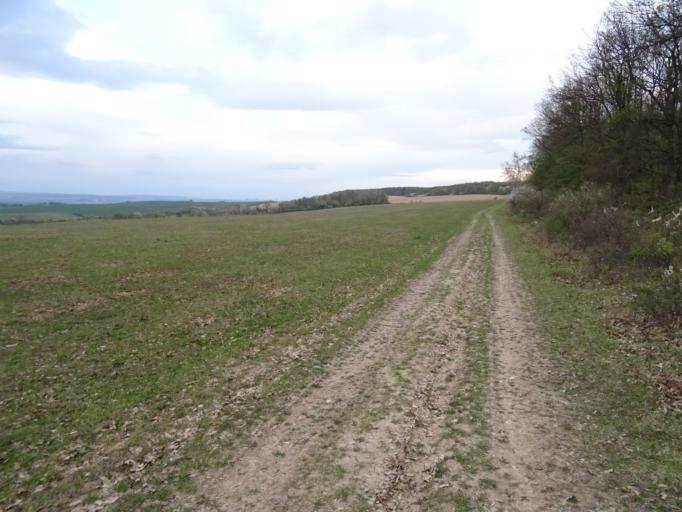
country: SK
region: Kosicky
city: Moldava nad Bodvou
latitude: 48.5274
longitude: 20.9956
